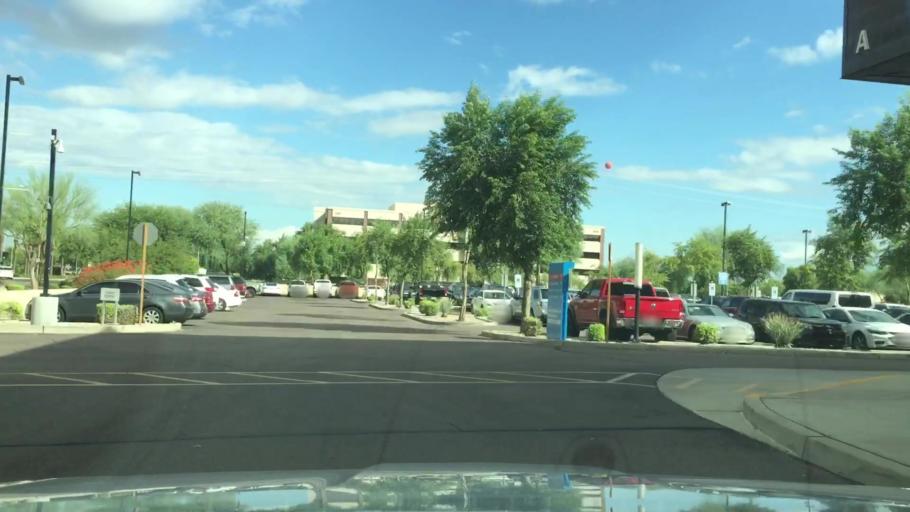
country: US
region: Arizona
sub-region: Maricopa County
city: Tolleson
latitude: 33.4784
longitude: -112.2591
